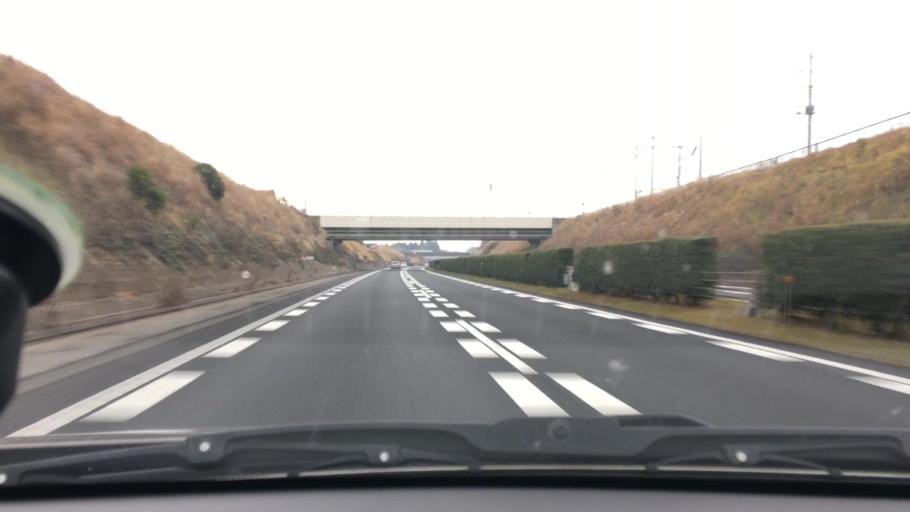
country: JP
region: Chiba
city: Narita
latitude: 35.8005
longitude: 140.3601
